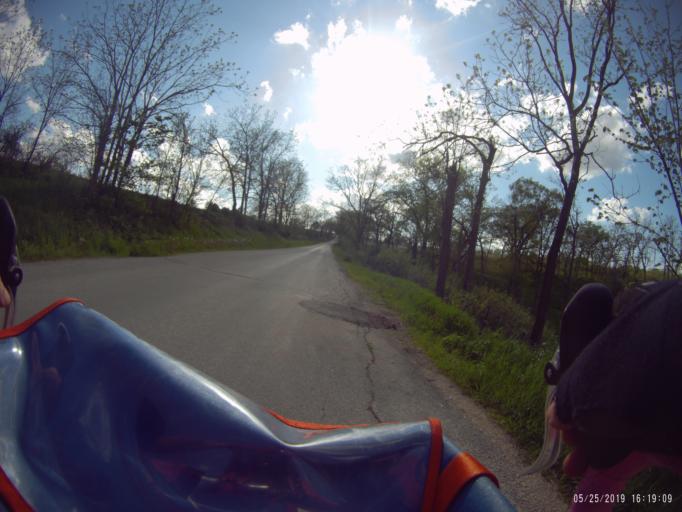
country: US
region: Wisconsin
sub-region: Dane County
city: Mount Horeb
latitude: 42.9665
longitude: -89.6969
